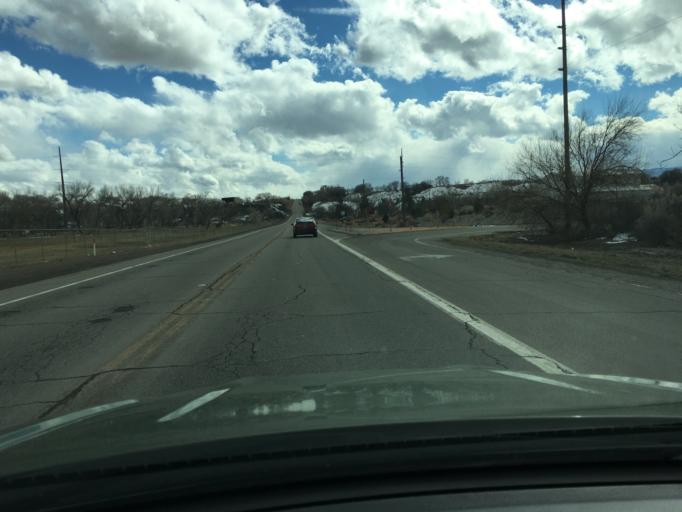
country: US
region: Colorado
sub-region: Mesa County
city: Clifton
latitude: 39.0595
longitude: -108.4595
